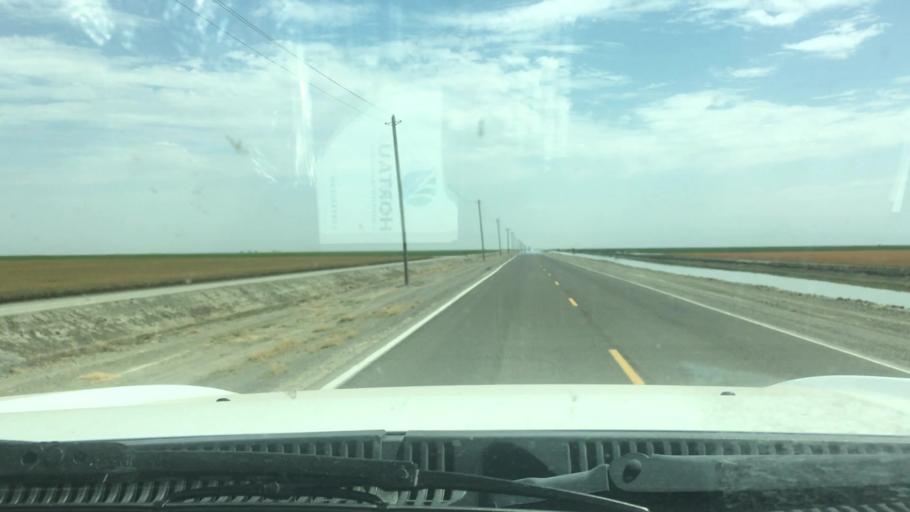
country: US
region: California
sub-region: Tulare County
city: Alpaugh
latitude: 35.9160
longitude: -119.5733
